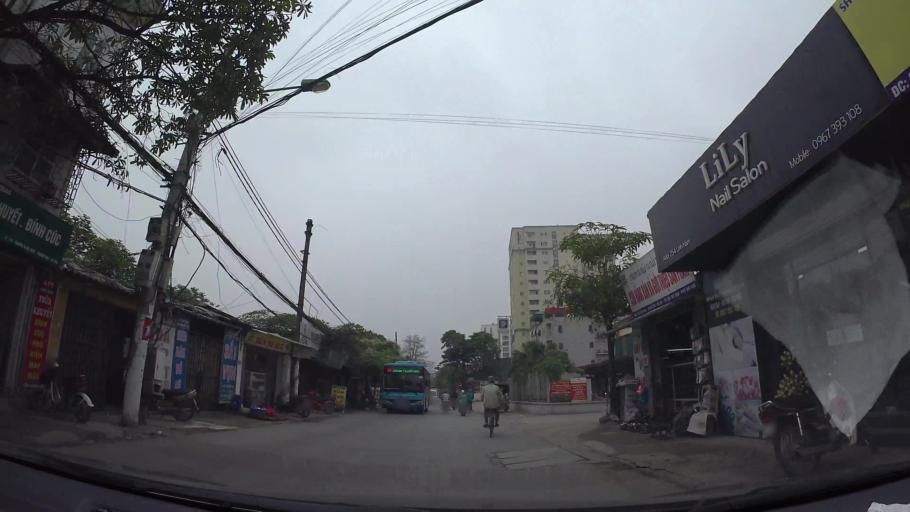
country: VN
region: Ha Noi
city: Hai BaTrung
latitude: 20.9826
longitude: 105.8782
